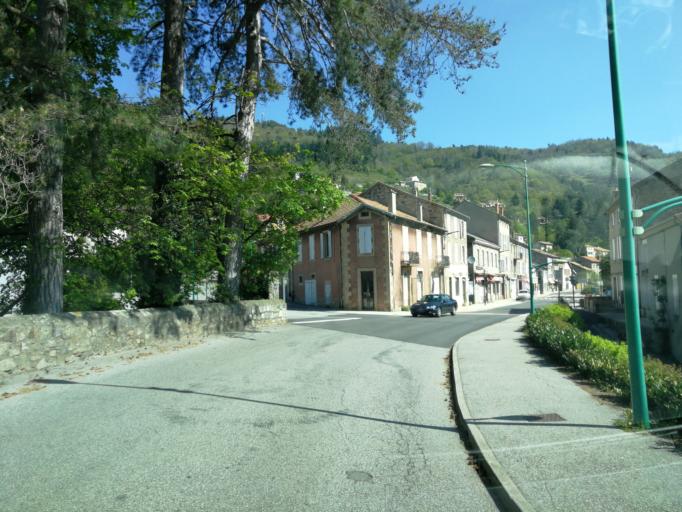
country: FR
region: Rhone-Alpes
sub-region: Departement de l'Ardeche
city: Le Cheylard
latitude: 44.9126
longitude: 4.4270
